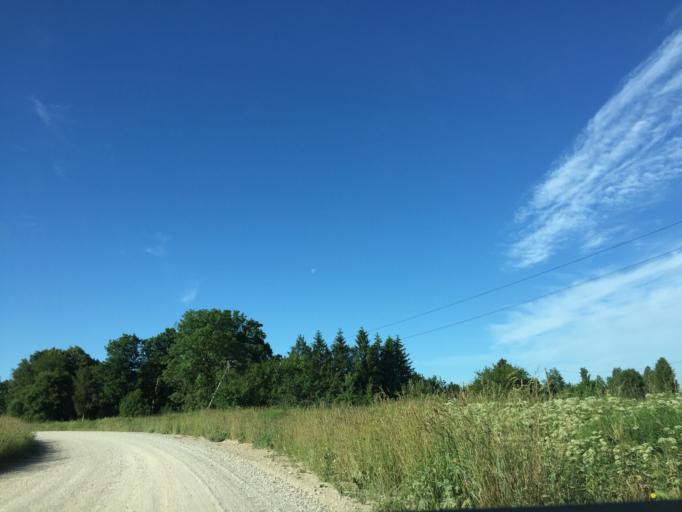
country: LV
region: Ventspils Rajons
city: Piltene
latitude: 57.3232
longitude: 21.6888
